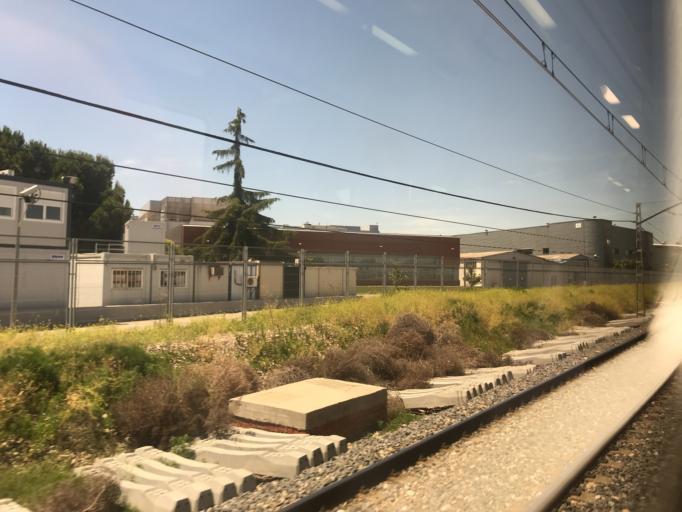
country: ES
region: Madrid
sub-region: Provincia de Madrid
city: Getafe
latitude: 40.2987
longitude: -3.7066
